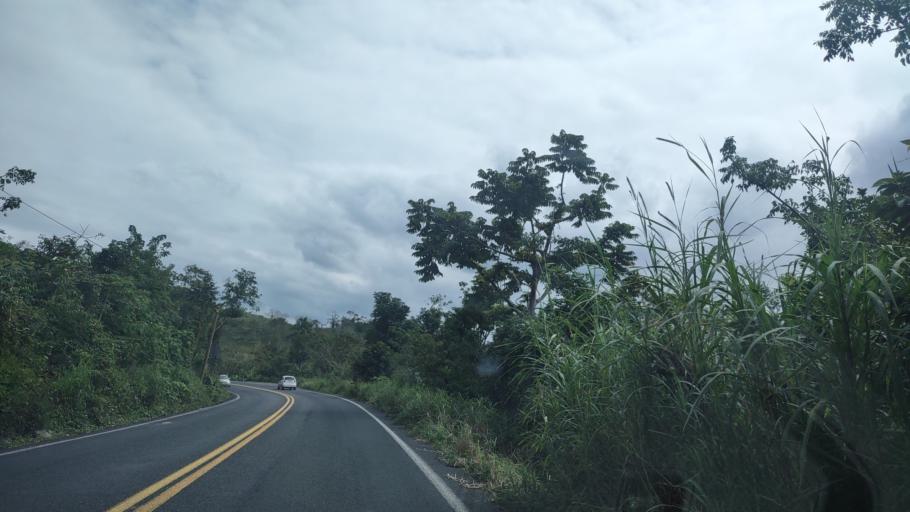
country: MX
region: Veracruz
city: Papantla de Olarte
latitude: 20.4625
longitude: -97.2690
